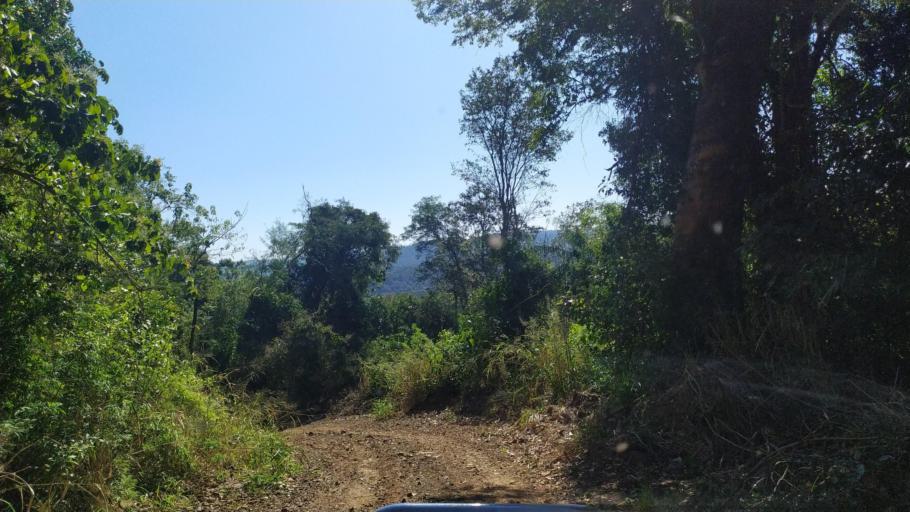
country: AR
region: Misiones
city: El Alcazar
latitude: -26.7603
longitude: -54.5779
